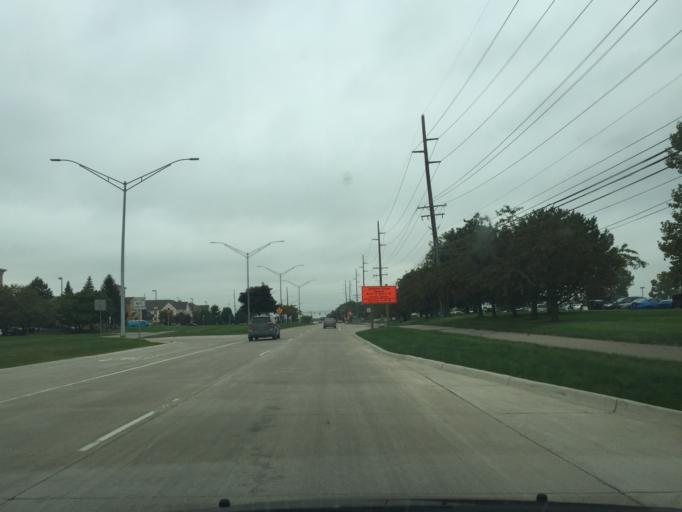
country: US
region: Michigan
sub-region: Oakland County
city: Auburn Hills
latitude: 42.6493
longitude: -83.2438
